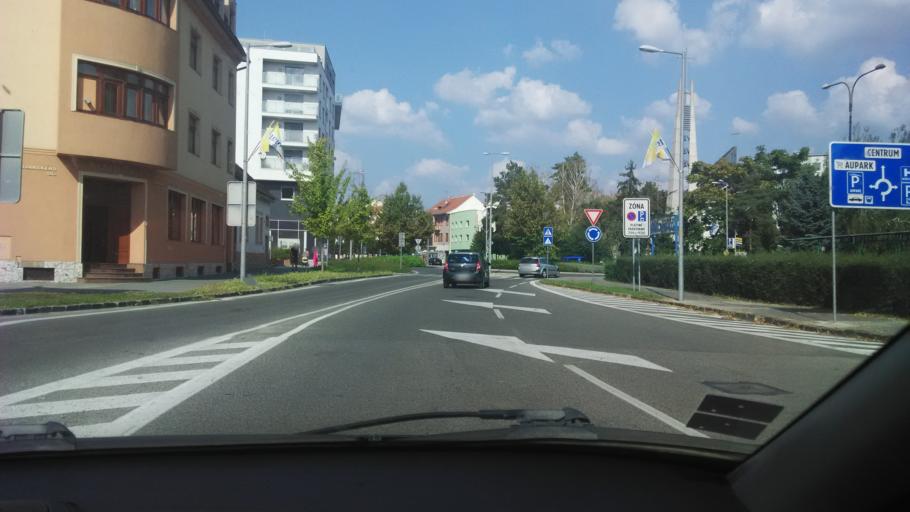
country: SK
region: Trnavsky
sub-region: Okres Trnava
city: Piestany
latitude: 48.5866
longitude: 17.8327
